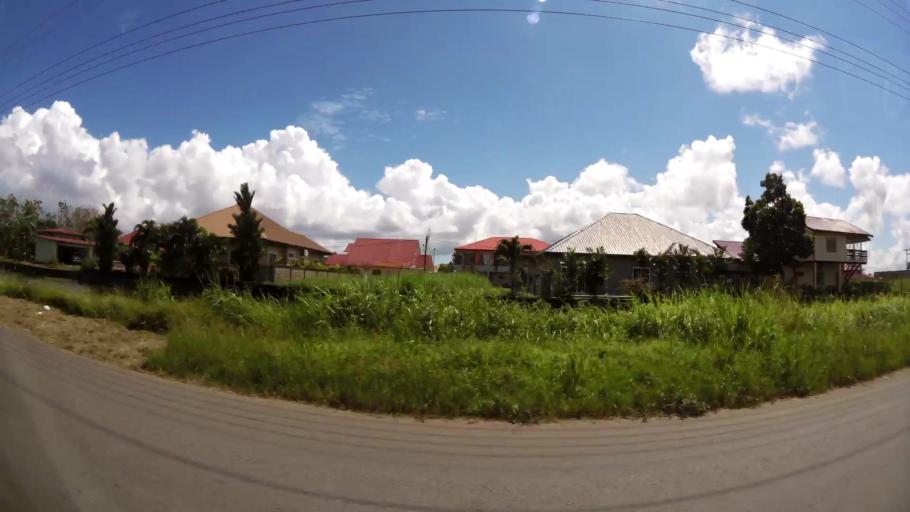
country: SR
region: Paramaribo
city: Paramaribo
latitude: 5.8626
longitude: -55.1351
